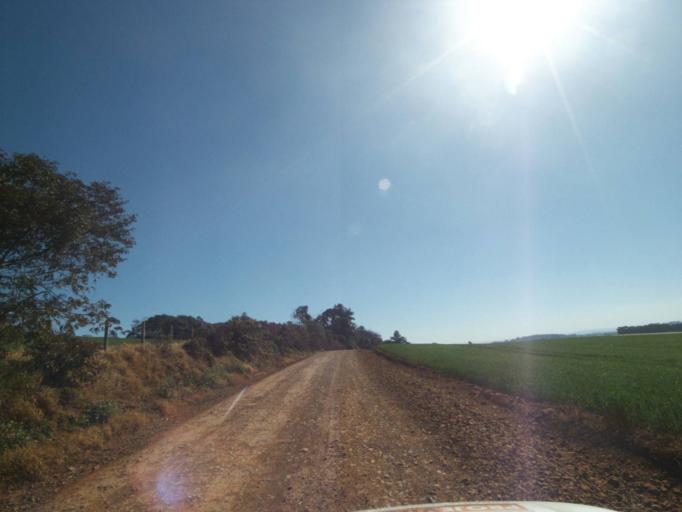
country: BR
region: Parana
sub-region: Tibagi
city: Tibagi
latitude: -24.5865
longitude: -50.6088
